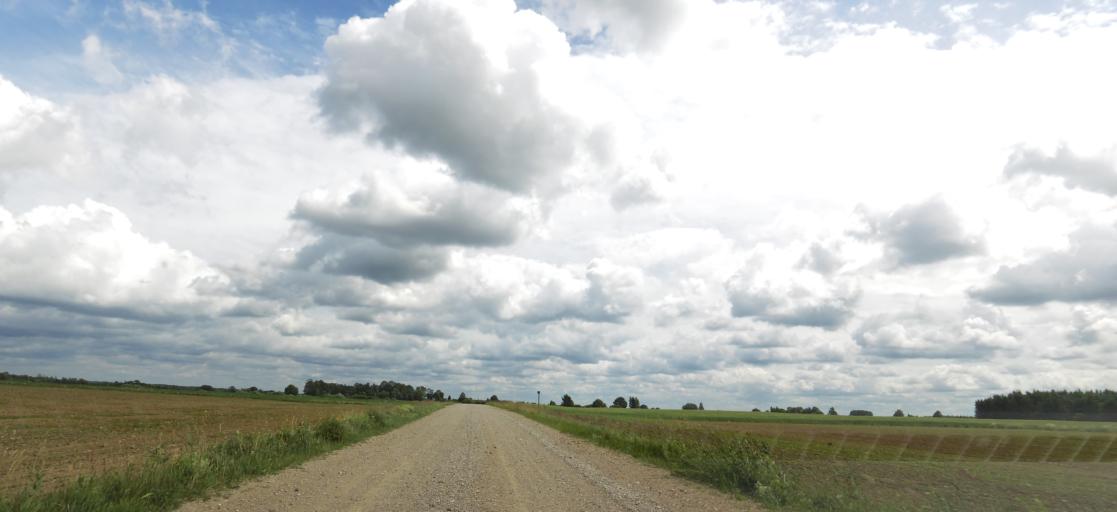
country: LT
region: Panevezys
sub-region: Birzai
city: Birzai
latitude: 56.3155
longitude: 24.7575
